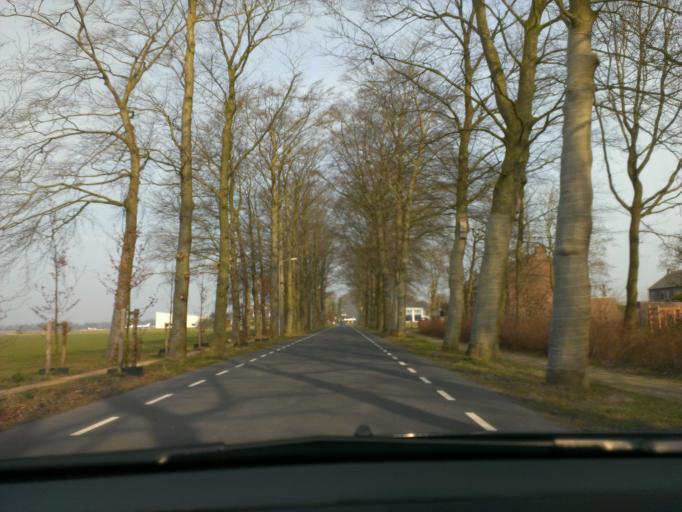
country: NL
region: Gelderland
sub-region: Gemeente Voorst
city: Twello
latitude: 52.2373
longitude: 6.0462
